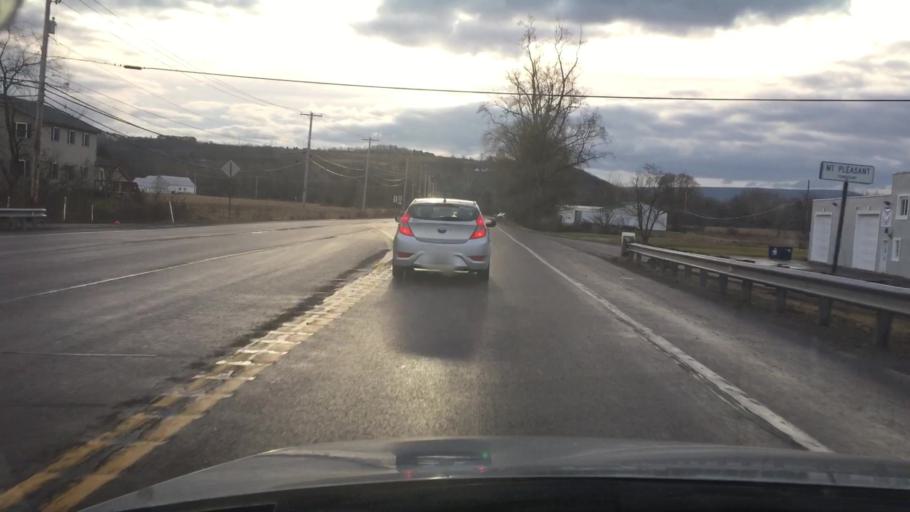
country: US
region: Pennsylvania
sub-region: Columbia County
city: Bloomsburg
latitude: 41.0264
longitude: -76.4797
